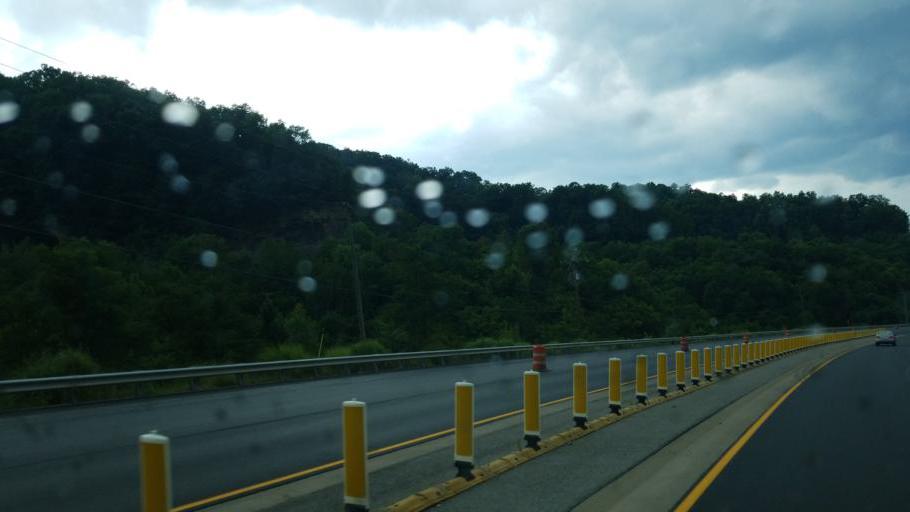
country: US
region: Kentucky
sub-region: Pike County
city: Pikeville
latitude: 37.5126
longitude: -82.4975
